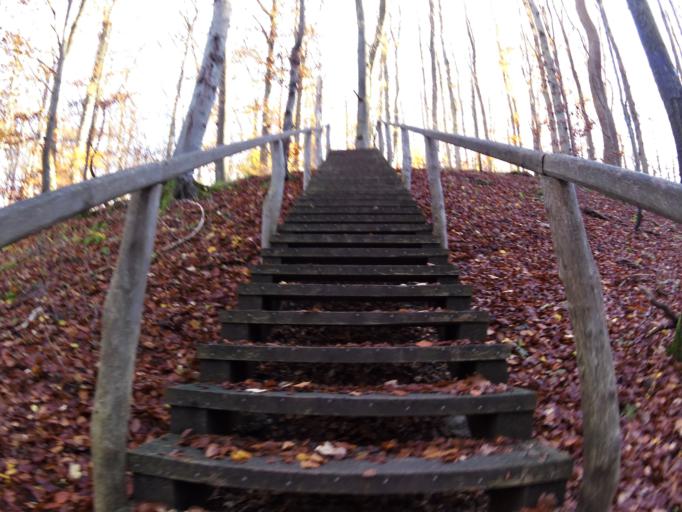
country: DE
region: Thuringia
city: Kammerforst
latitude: 51.0677
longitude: 10.4424
